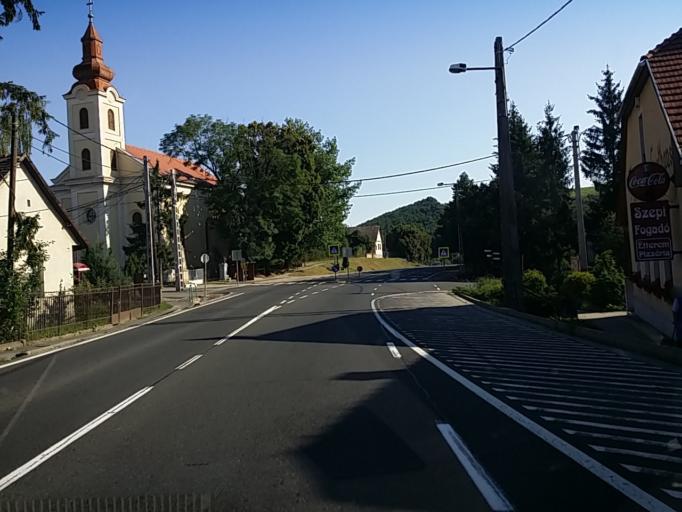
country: HU
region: Pest
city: Veroce
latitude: 47.8556
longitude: 19.1047
